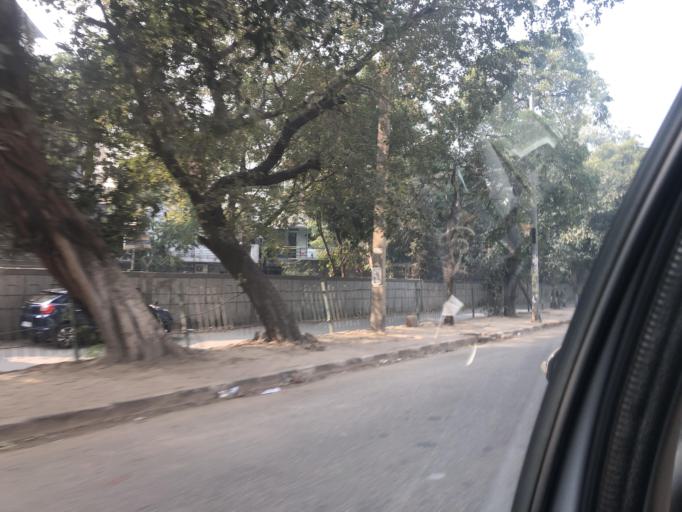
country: IN
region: NCT
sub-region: North West Delhi
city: Pitampura
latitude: 28.6782
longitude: 77.1044
